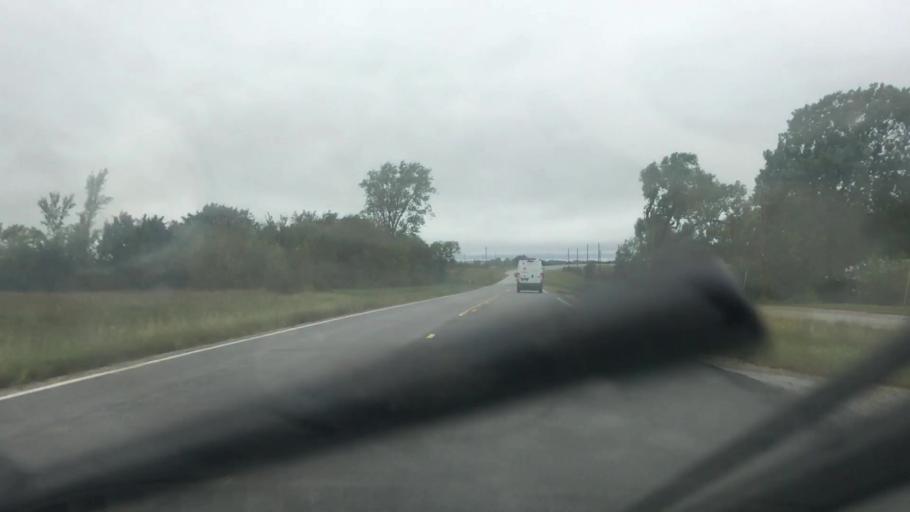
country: US
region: Kansas
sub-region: Anderson County
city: Garnett
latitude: 38.1663
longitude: -95.2934
